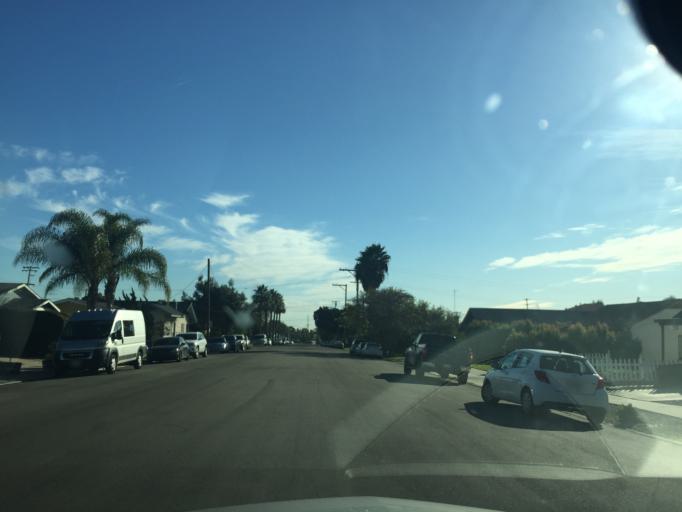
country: US
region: California
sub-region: San Diego County
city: San Diego
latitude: 32.7524
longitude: -117.1205
